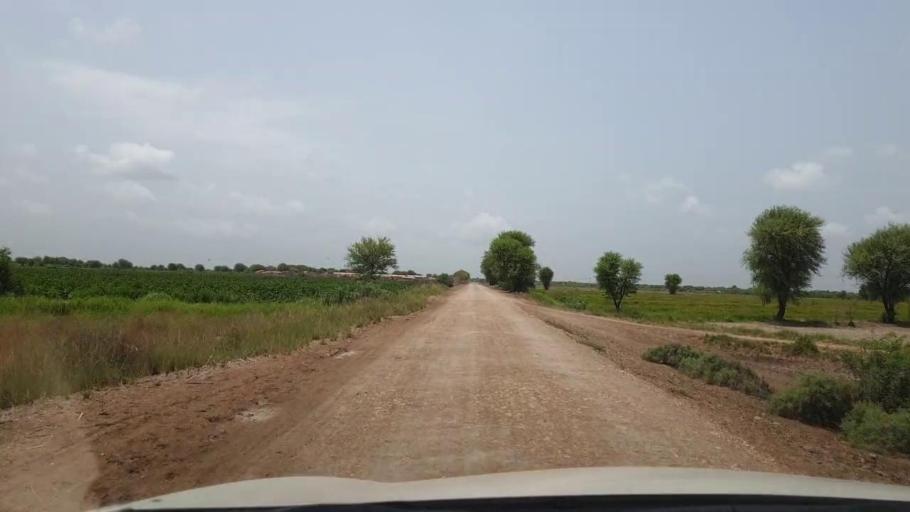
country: PK
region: Sindh
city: Chambar
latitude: 25.2075
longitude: 68.7658
